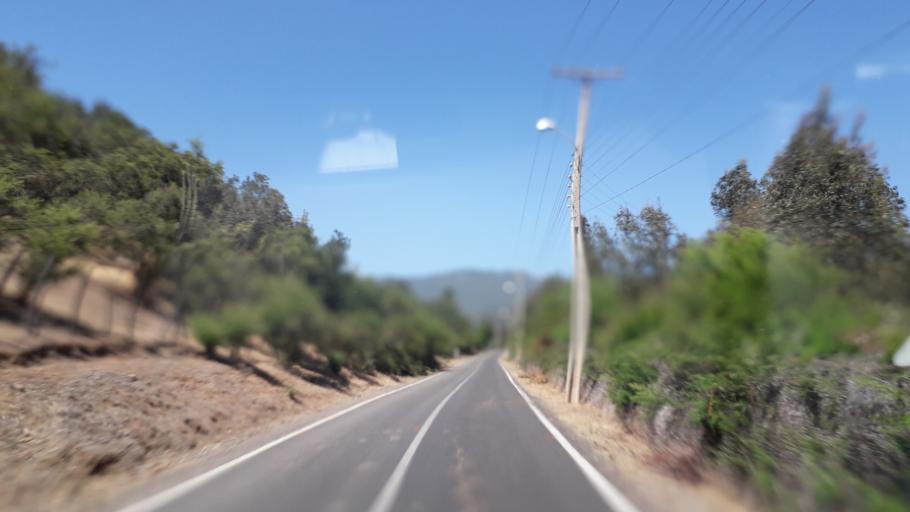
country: CL
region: Valparaiso
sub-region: Provincia de Marga Marga
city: Limache
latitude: -33.0806
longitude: -71.2117
